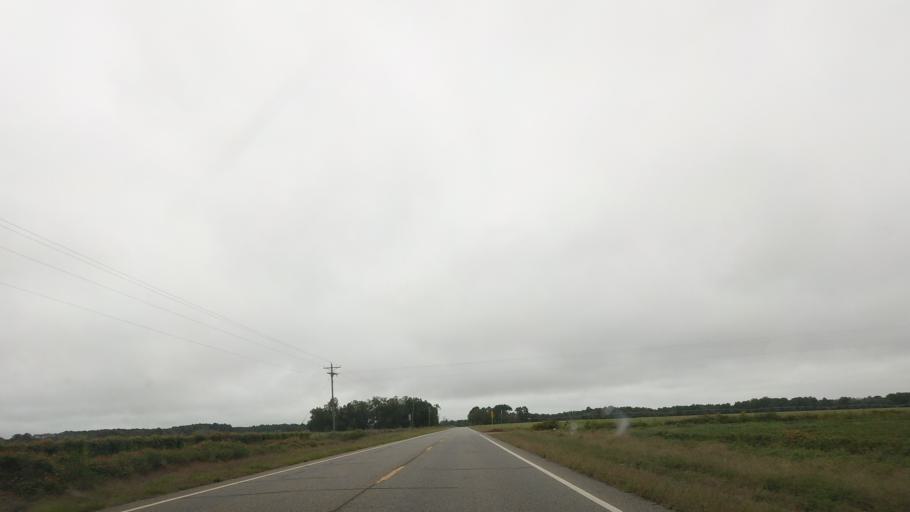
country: US
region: Georgia
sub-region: Irwin County
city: Ocilla
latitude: 31.5234
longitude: -83.2447
